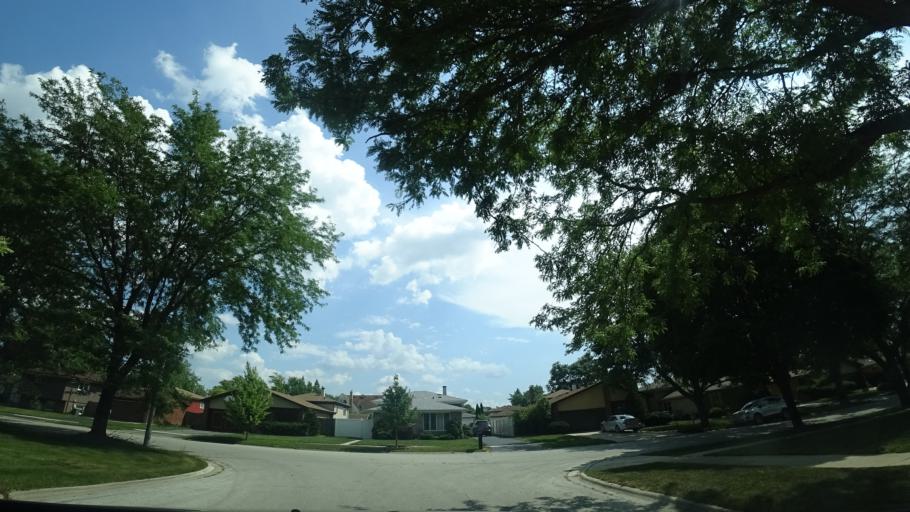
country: US
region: Illinois
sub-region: Cook County
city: Merrionette Park
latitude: 41.6737
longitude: -87.7157
